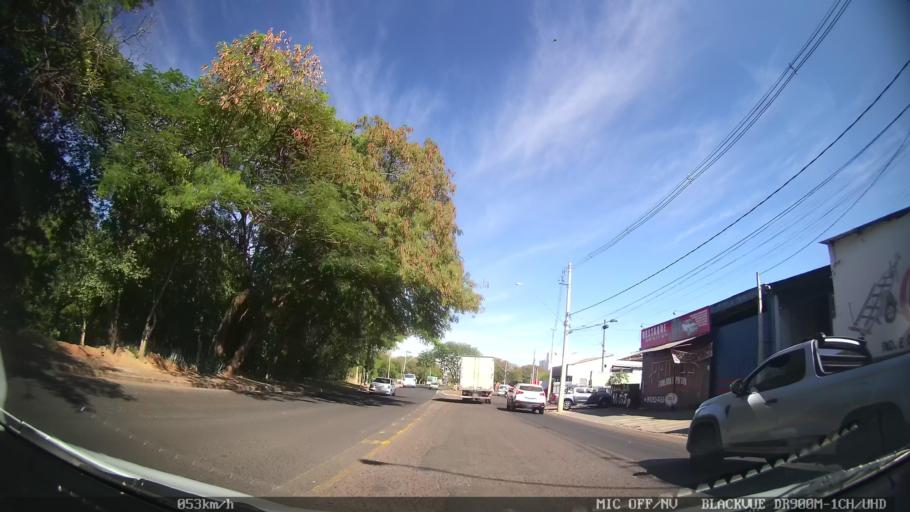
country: BR
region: Sao Paulo
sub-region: Sao Jose Do Rio Preto
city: Sao Jose do Rio Preto
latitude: -20.7969
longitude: -49.3994
